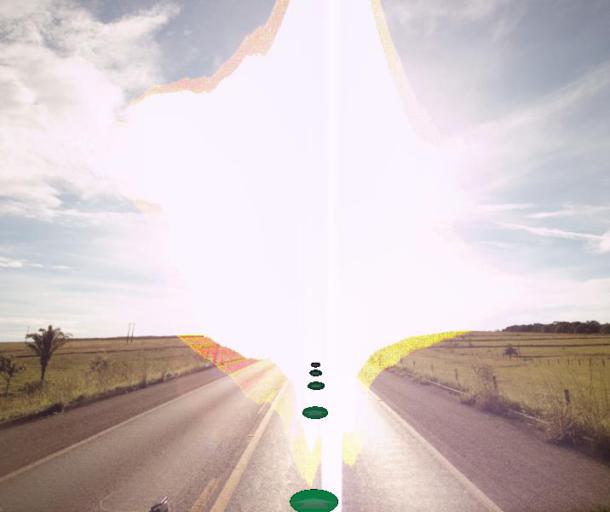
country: BR
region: Goias
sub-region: Abadiania
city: Abadiania
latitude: -15.7698
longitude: -48.4576
